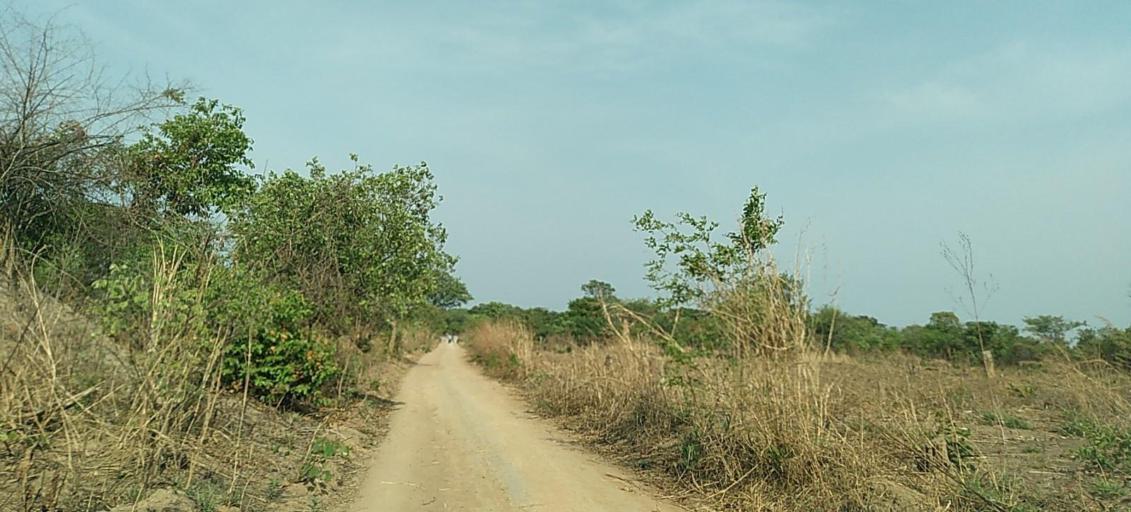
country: ZM
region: Copperbelt
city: Luanshya
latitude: -13.2194
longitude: 28.6597
